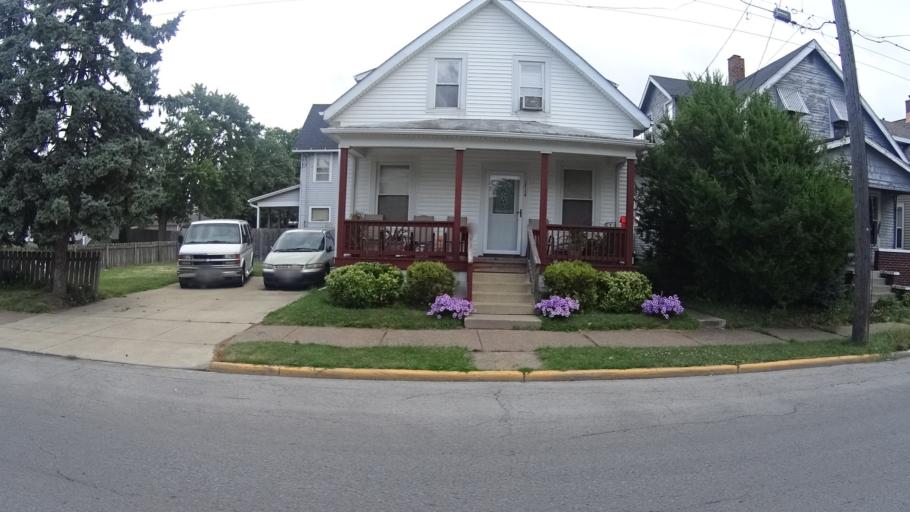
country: US
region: Ohio
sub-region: Erie County
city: Sandusky
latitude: 41.4425
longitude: -82.7202
